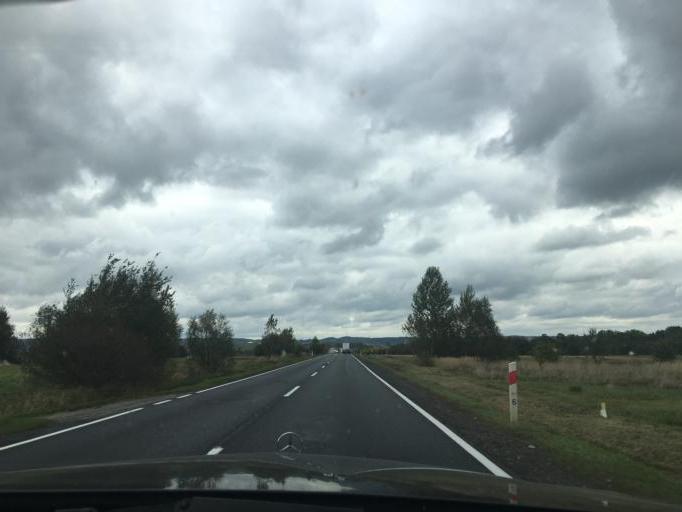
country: PL
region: Subcarpathian Voivodeship
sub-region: Powiat krosnienski
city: Kroscienko Wyzne
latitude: 49.6646
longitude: 21.8403
